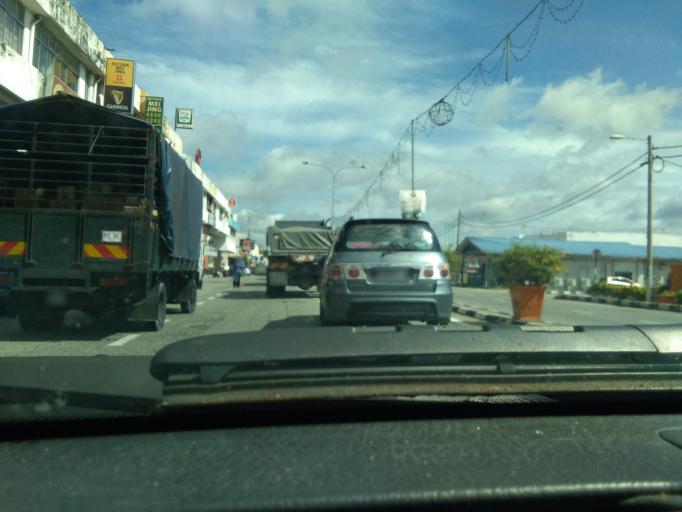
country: MY
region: Perak
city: Bagan Serai
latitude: 5.0125
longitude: 100.5342
